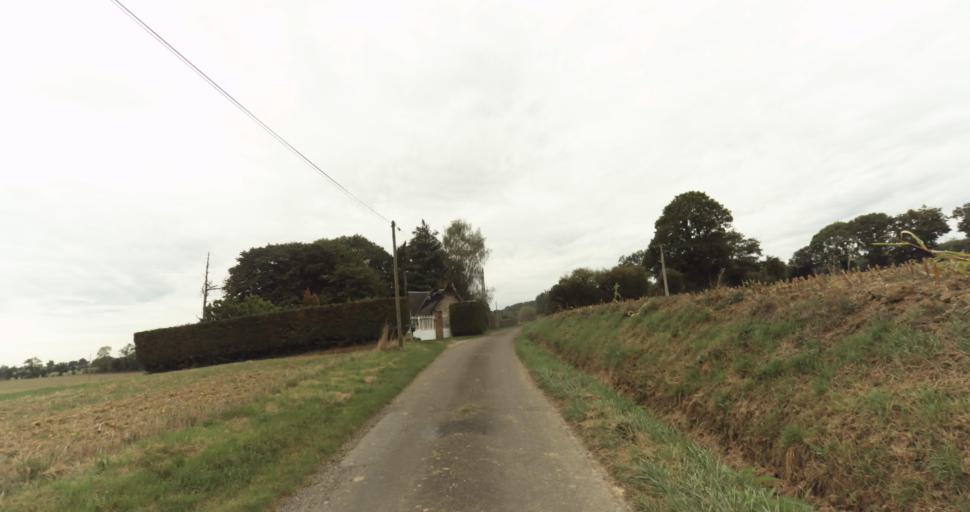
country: FR
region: Lower Normandy
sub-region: Departement de l'Orne
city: Gace
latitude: 48.6872
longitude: 0.2725
